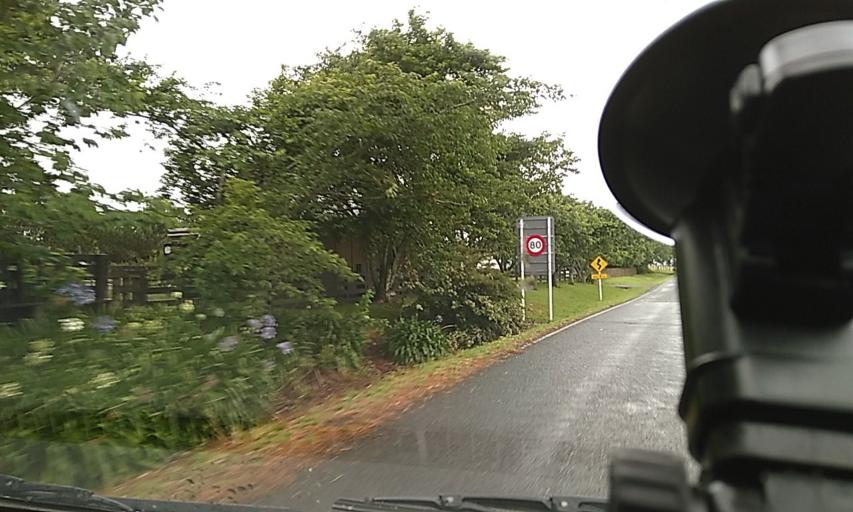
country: NZ
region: Auckland
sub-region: Auckland
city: Pukekohe East
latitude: -37.3240
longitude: 174.9180
